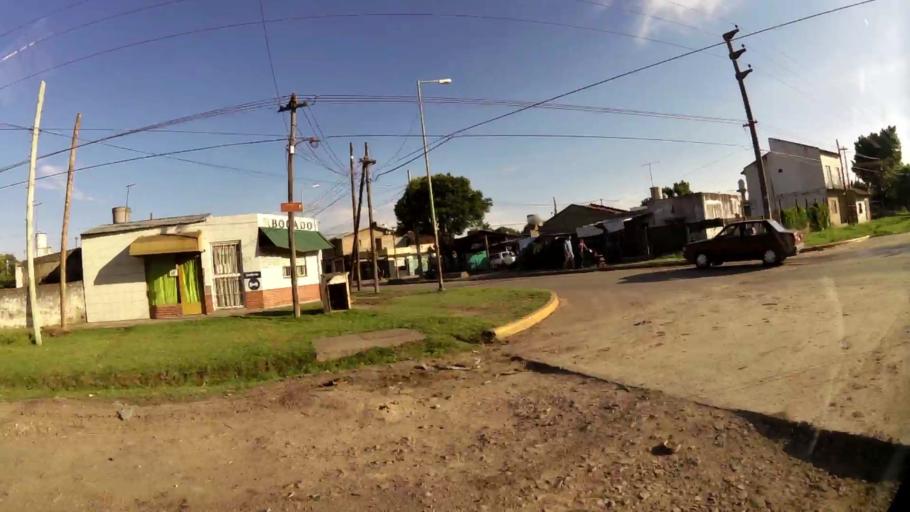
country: AR
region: Buenos Aires
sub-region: Partido de Merlo
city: Merlo
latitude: -34.6918
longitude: -58.7469
